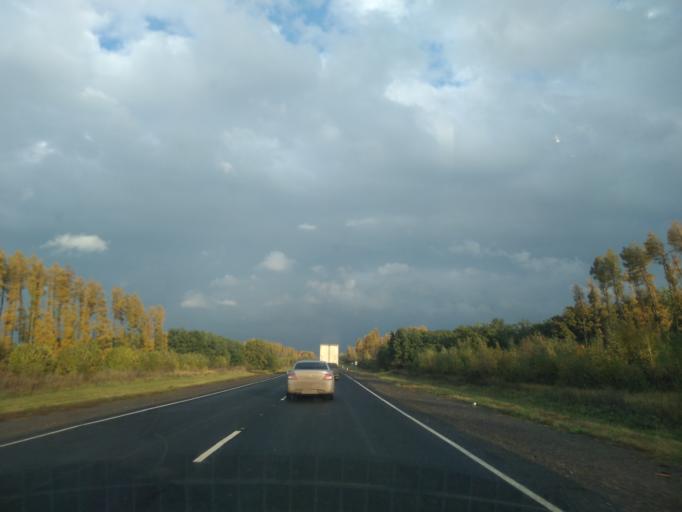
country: RU
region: Lipetsk
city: Donskoye
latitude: 52.5861
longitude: 38.8493
